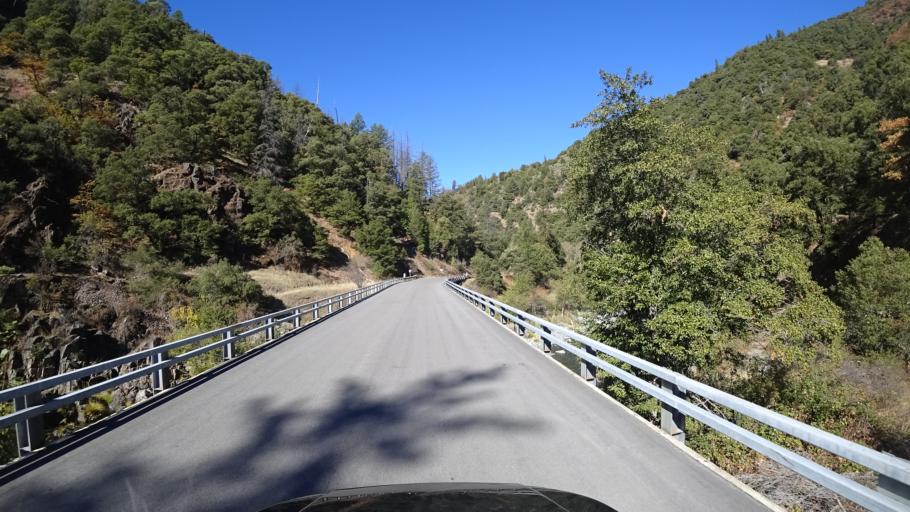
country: US
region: California
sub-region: Humboldt County
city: Willow Creek
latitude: 41.2329
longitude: -123.2601
